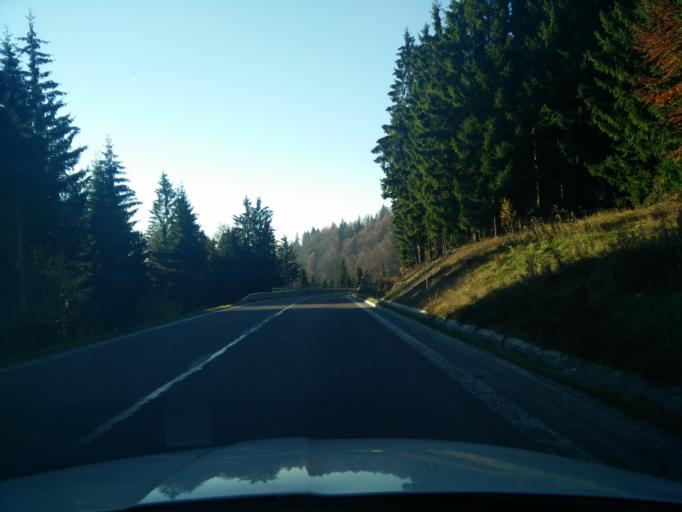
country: SK
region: Zilinsky
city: Oravska Lesna
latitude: 49.3676
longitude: 19.1140
